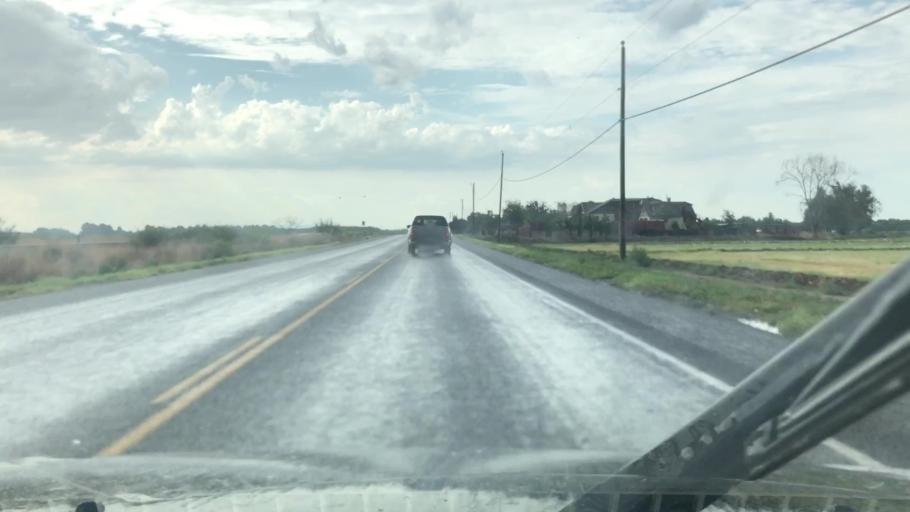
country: US
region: New Mexico
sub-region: Dona Ana County
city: Mesquite
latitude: 32.1860
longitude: -106.7101
